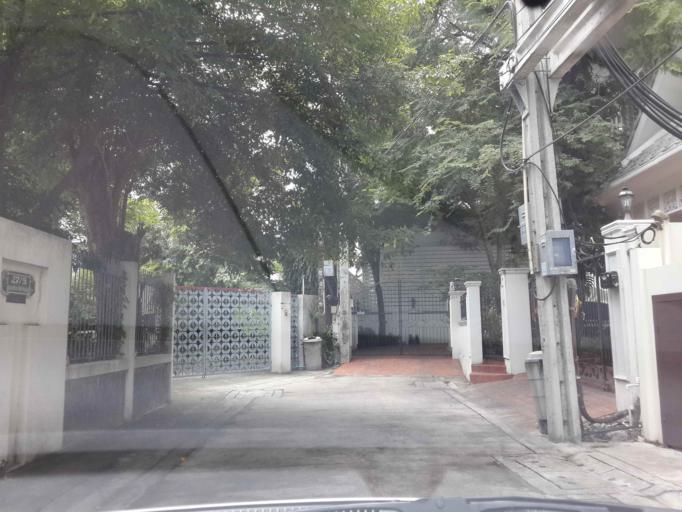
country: TH
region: Bangkok
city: Watthana
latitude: 13.7385
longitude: 100.5680
